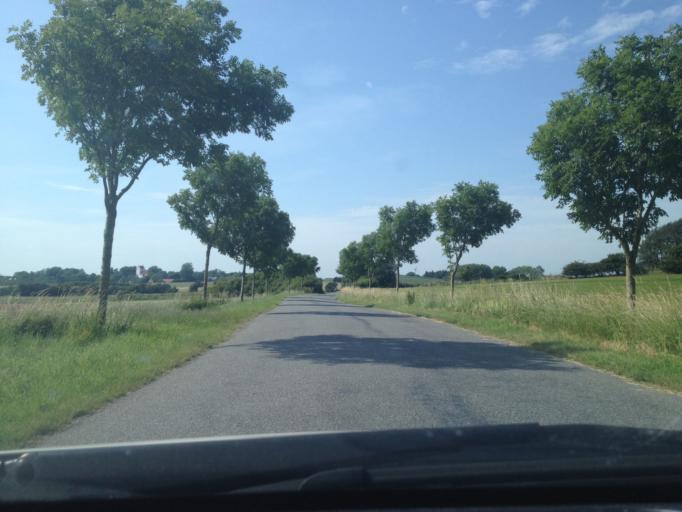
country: DK
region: Central Jutland
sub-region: Samso Kommune
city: Tranebjerg
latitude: 55.7948
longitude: 10.5711
